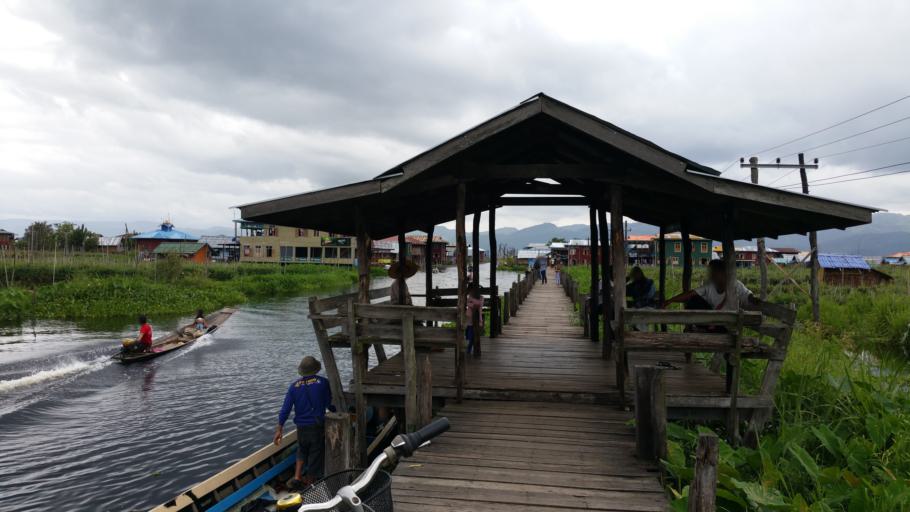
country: MM
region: Shan
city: Taunggyi
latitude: 20.5812
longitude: 96.9361
